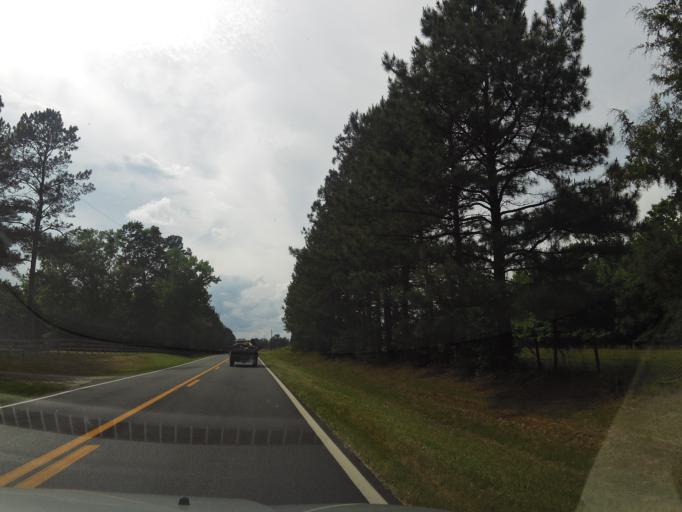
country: US
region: Georgia
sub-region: McDuffie County
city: Thomson
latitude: 33.5360
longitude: -82.4957
